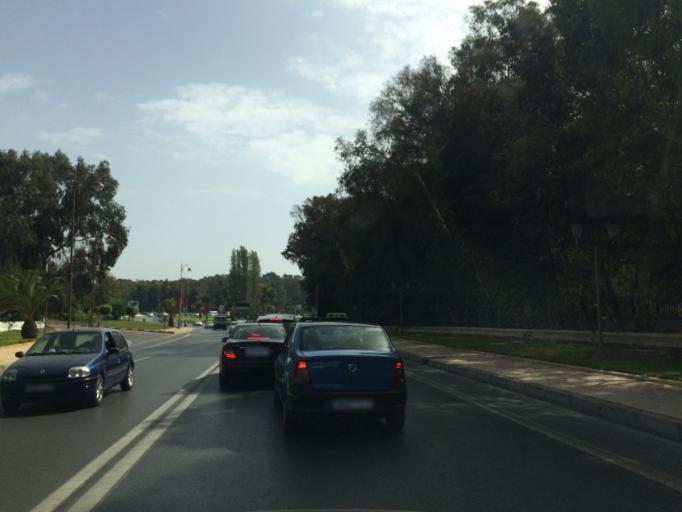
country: MA
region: Rabat-Sale-Zemmour-Zaer
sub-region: Rabat
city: Rabat
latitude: 33.9953
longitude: -6.8376
